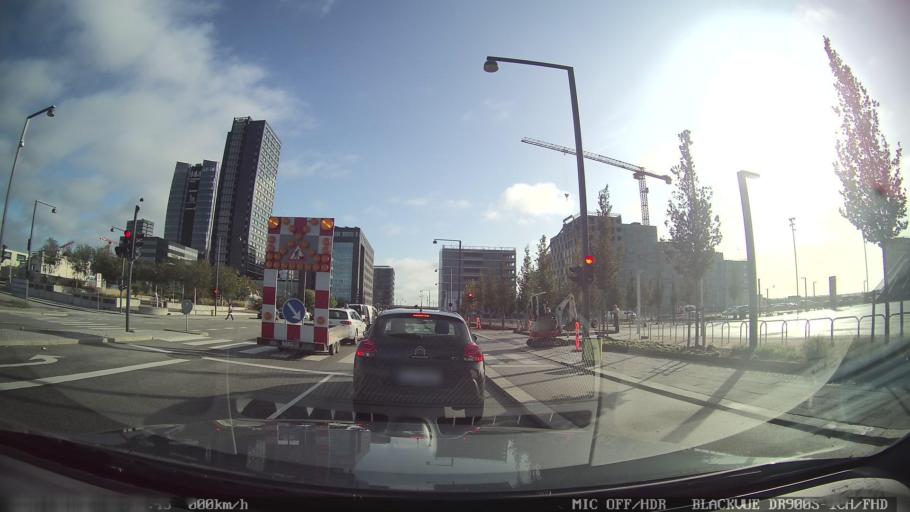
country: DK
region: Capital Region
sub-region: Tarnby Kommune
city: Tarnby
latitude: 55.6263
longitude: 12.5741
